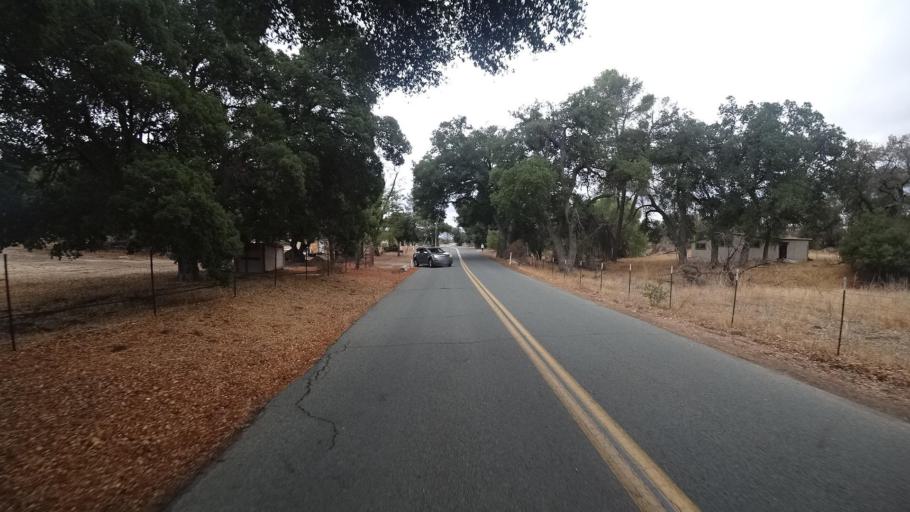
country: US
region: California
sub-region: San Diego County
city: Campo
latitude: 32.6231
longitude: -116.3224
